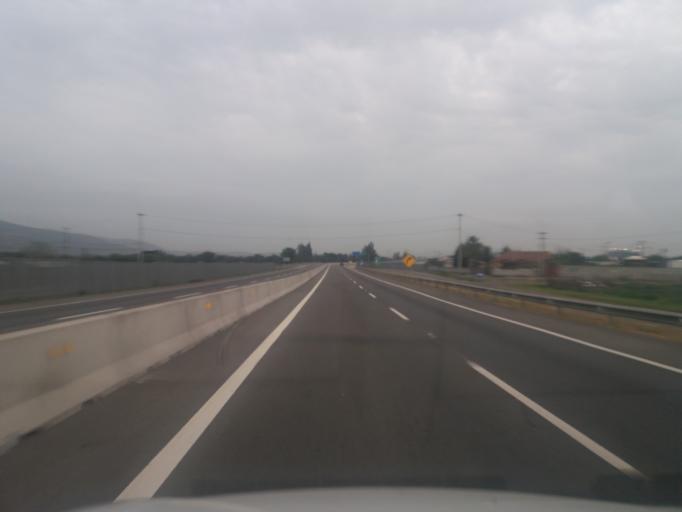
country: CL
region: Valparaiso
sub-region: Provincia de Quillota
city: Quillota
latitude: -32.9007
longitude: -71.2422
